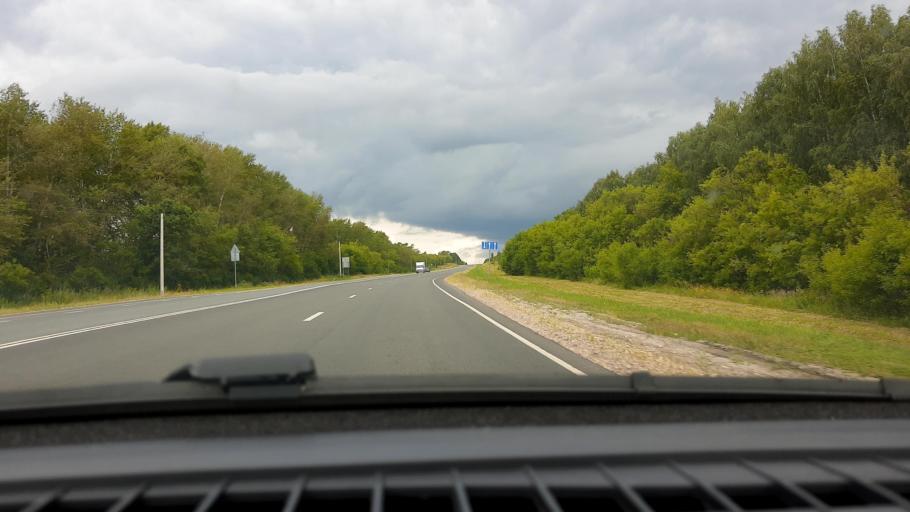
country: RU
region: Nizjnij Novgorod
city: Bol'shoye Murashkino
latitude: 55.8030
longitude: 44.7640
